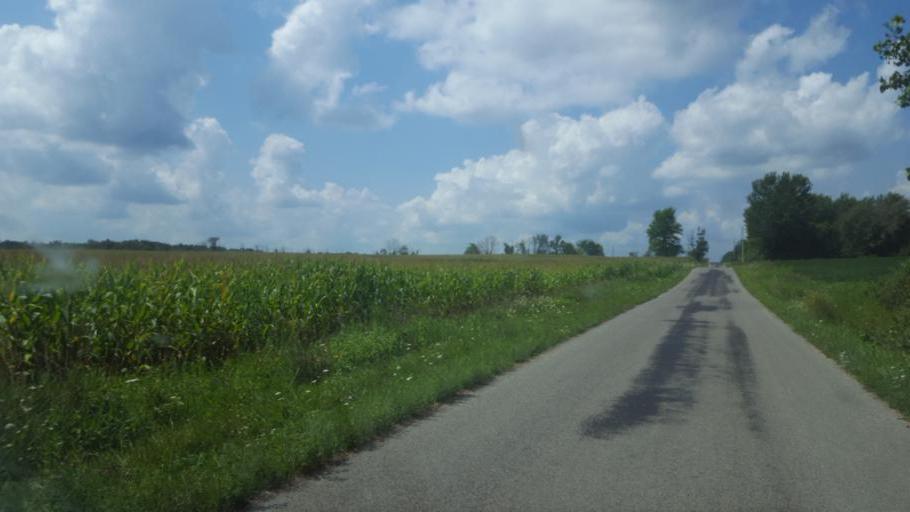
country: US
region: Ohio
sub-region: Knox County
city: Centerburg
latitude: 40.3845
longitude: -82.6781
